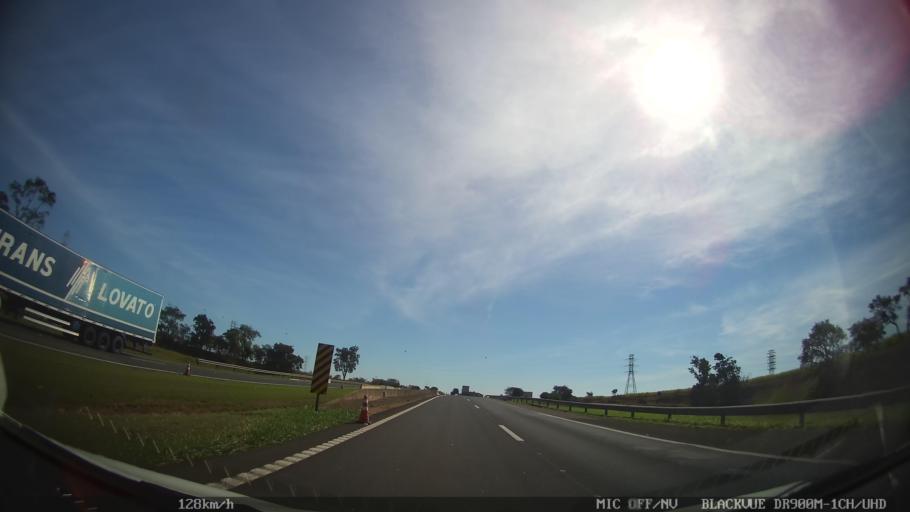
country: BR
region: Sao Paulo
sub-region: Porto Ferreira
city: Porto Ferreira
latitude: -21.9111
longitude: -47.4753
